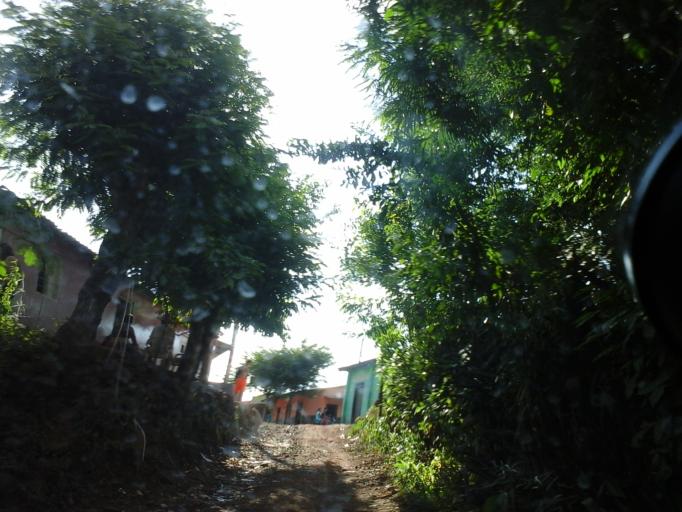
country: CO
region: Cesar
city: San Diego
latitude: 10.2425
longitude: -73.1380
